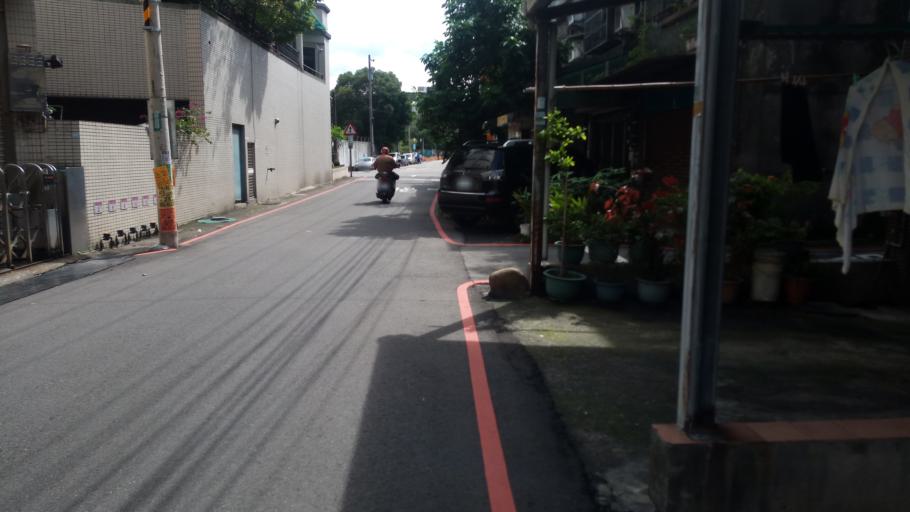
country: TW
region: Taiwan
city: Taoyuan City
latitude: 24.9417
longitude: 121.2500
